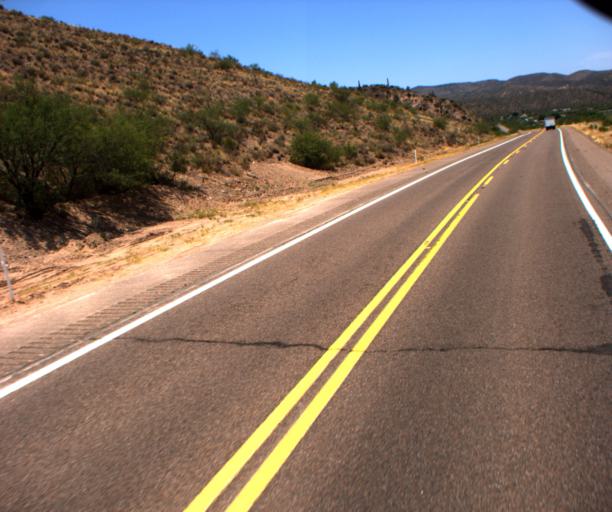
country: US
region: Arizona
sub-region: Gila County
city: Tonto Basin
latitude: 33.9505
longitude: -111.3229
